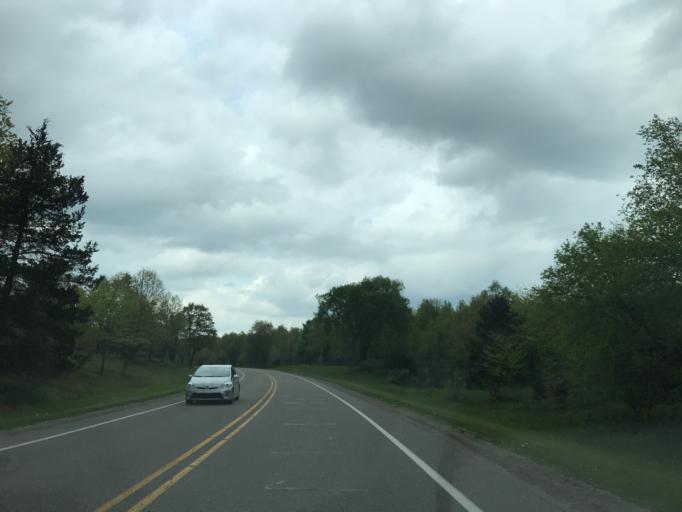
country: US
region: Michigan
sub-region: Oakland County
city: Milford
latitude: 42.5372
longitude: -83.6287
